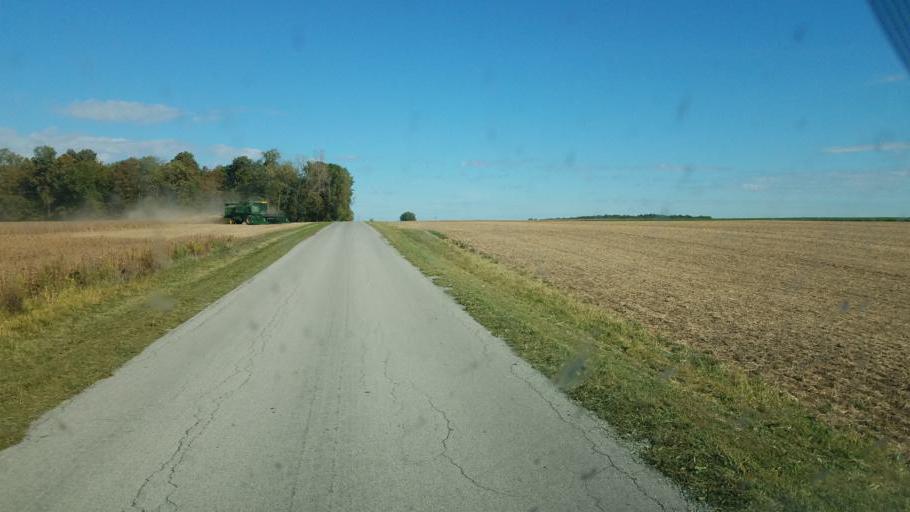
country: US
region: Ohio
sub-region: Wyandot County
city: Upper Sandusky
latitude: 40.7942
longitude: -83.2173
